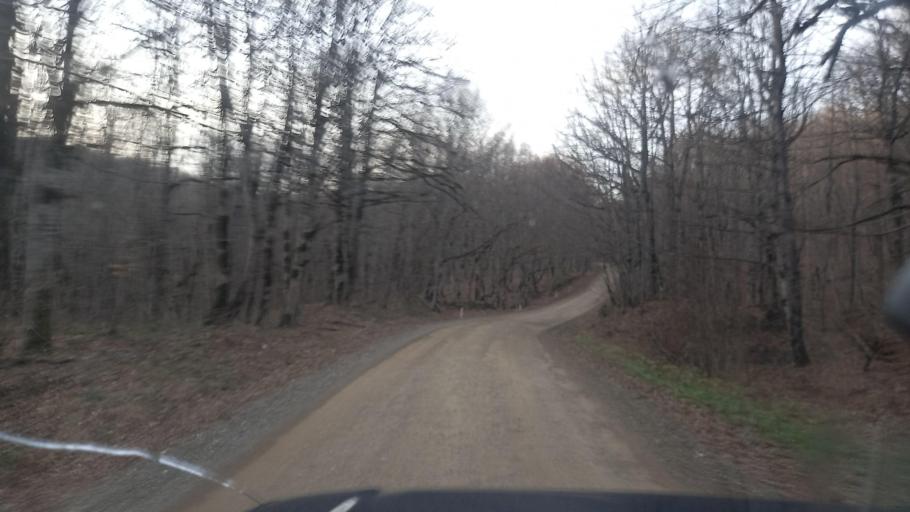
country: RU
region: Krasnodarskiy
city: Agoy
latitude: 44.3502
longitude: 39.2265
